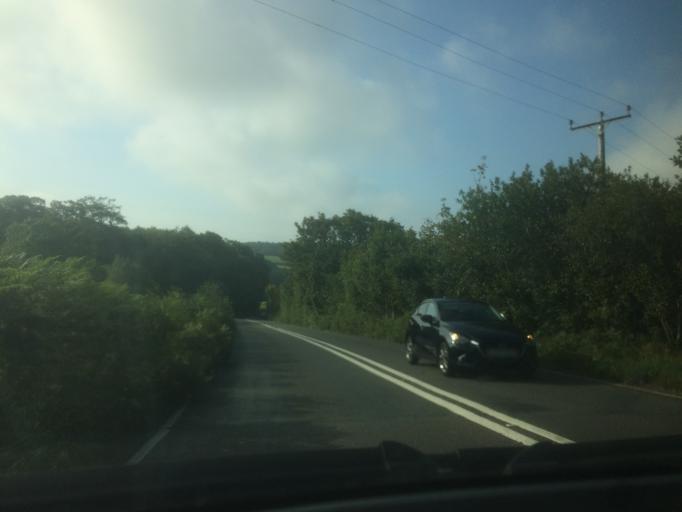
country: GB
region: England
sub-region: Cornwall
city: Gunnislake
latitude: 50.5352
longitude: -4.2000
